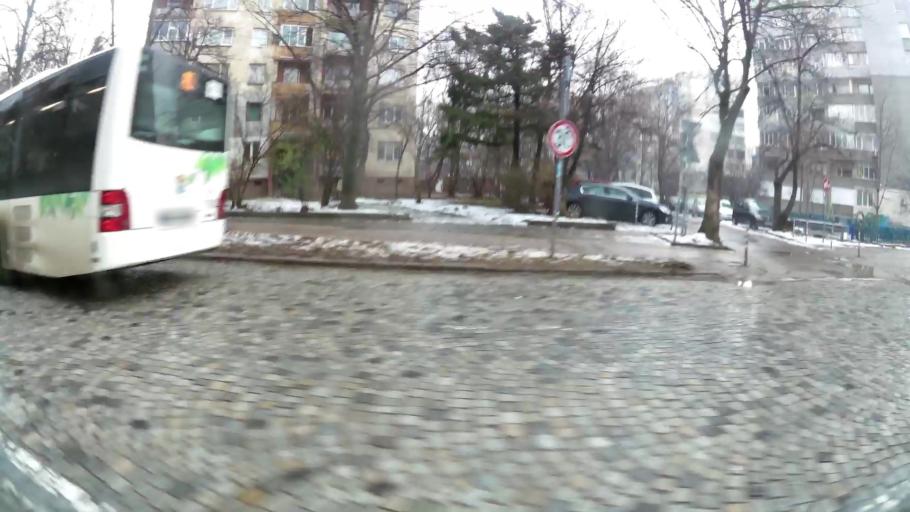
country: BG
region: Sofia-Capital
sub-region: Stolichna Obshtina
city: Sofia
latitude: 42.6688
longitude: 23.2983
